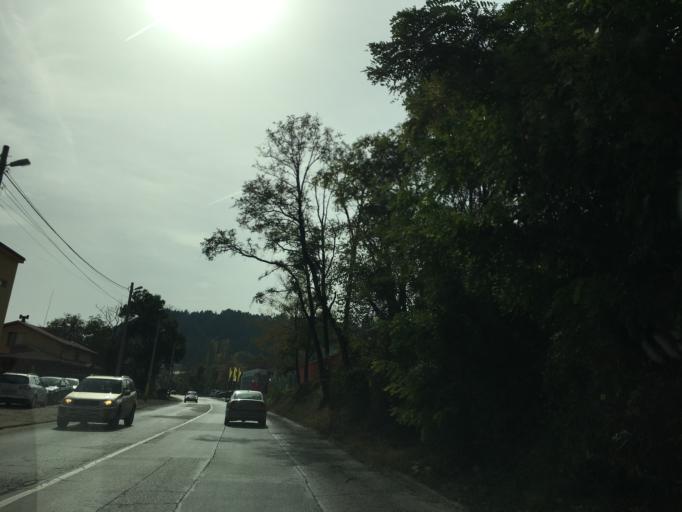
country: BG
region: Sofia-Capital
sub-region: Stolichna Obshtina
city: Sofia
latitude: 42.6113
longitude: 23.3994
